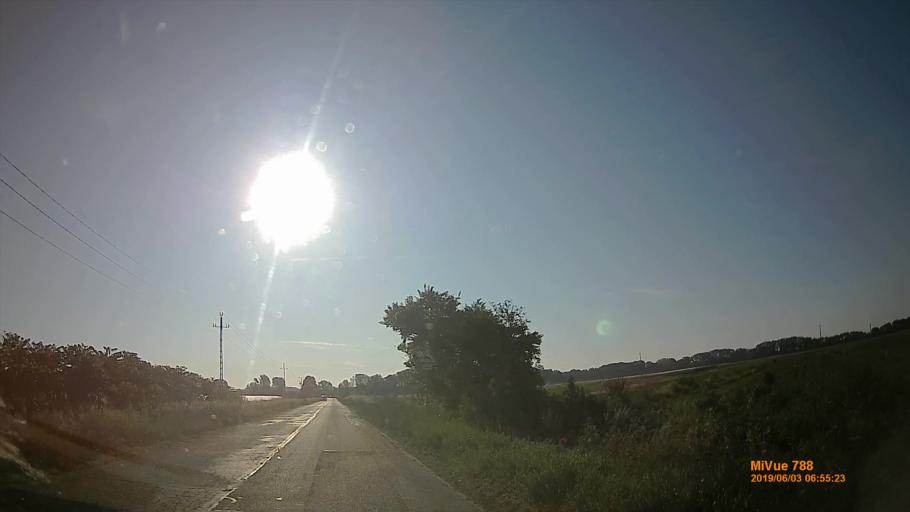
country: HU
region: Pest
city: Dabas
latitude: 47.2163
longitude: 19.2427
